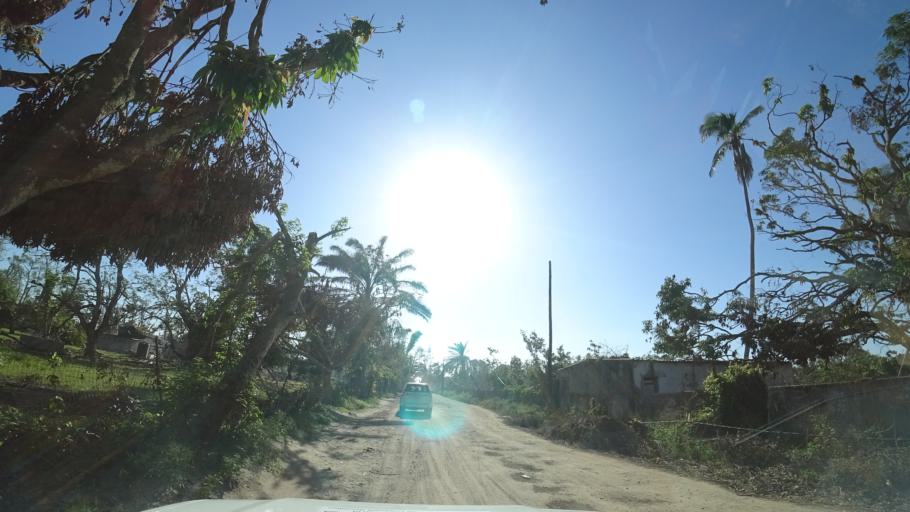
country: MZ
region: Sofala
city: Beira
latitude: -19.7665
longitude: 34.8942
